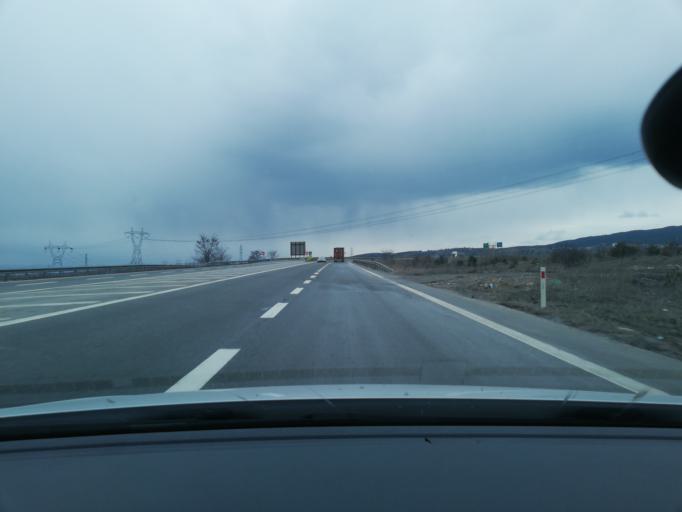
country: TR
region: Bolu
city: Gerede
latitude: 40.7765
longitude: 32.2144
